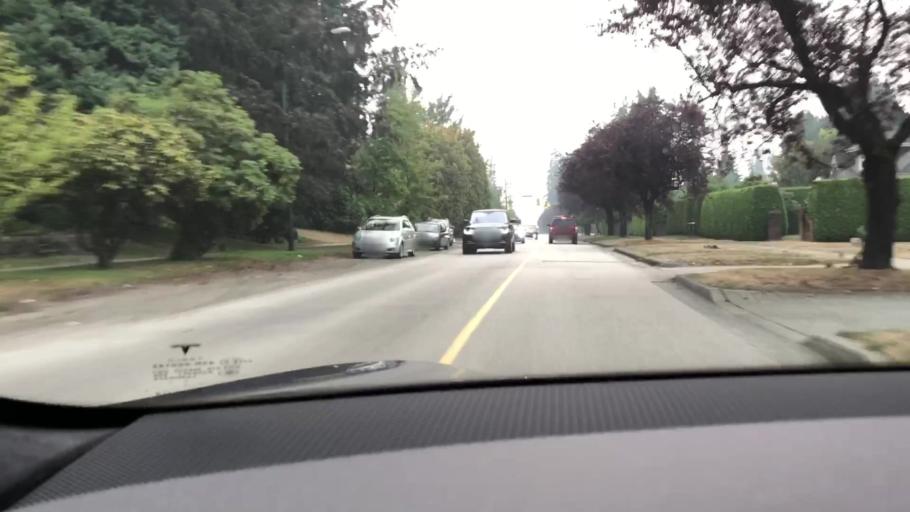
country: CA
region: British Columbia
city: Vancouver
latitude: 49.2418
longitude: -123.1372
